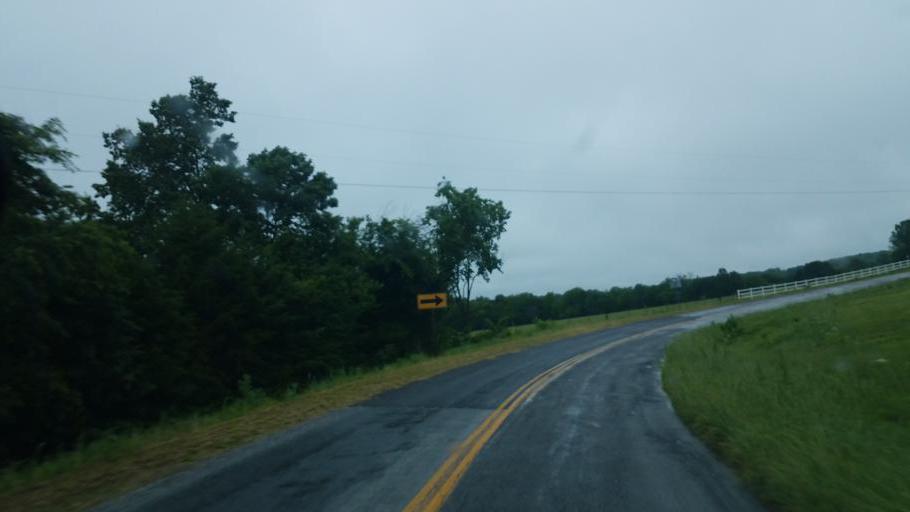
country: US
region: Missouri
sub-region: Moniteau County
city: California
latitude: 38.6891
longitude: -92.5885
